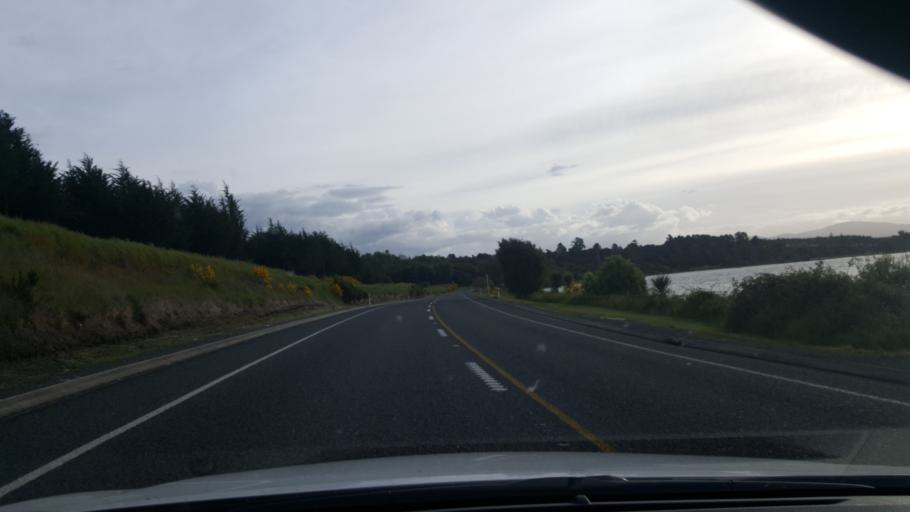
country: NZ
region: Waikato
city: Turangi
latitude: -38.9016
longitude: 175.9436
